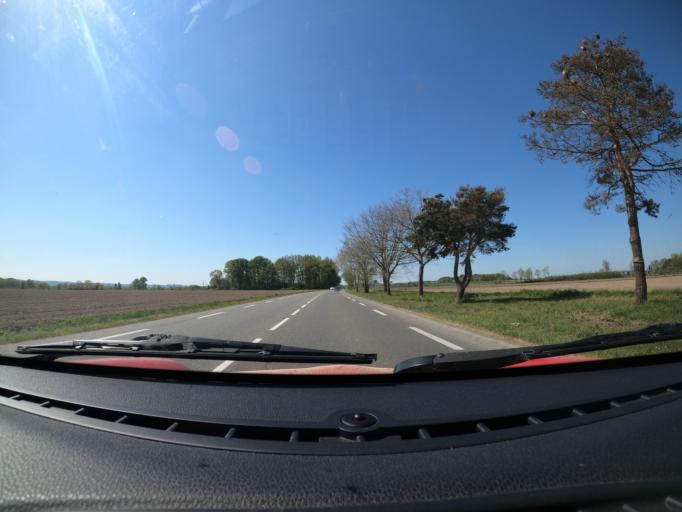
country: FR
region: Aquitaine
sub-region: Departement des Pyrenees-Atlantiques
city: Lescar
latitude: 43.3419
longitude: -0.4096
